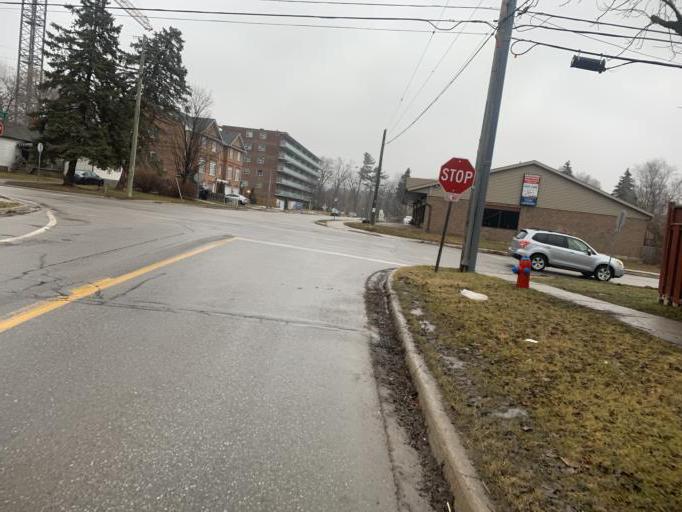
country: CA
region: Ontario
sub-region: Halton
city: Milton
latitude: 43.6602
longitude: -79.9172
